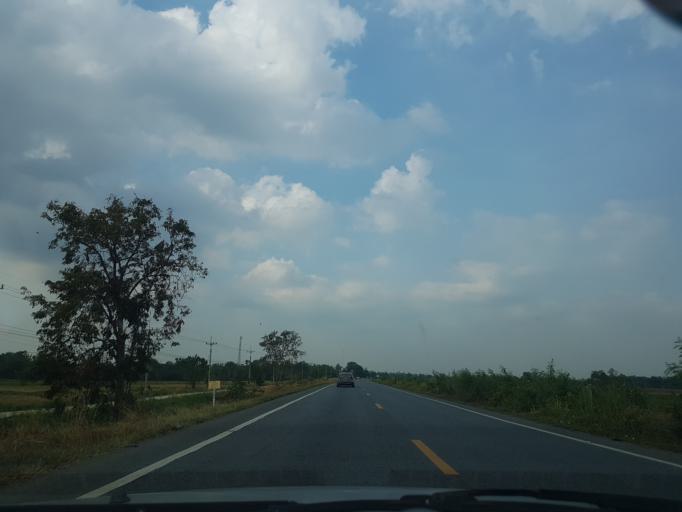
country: TH
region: Phra Nakhon Si Ayutthaya
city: Phachi
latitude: 14.4849
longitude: 100.7391
